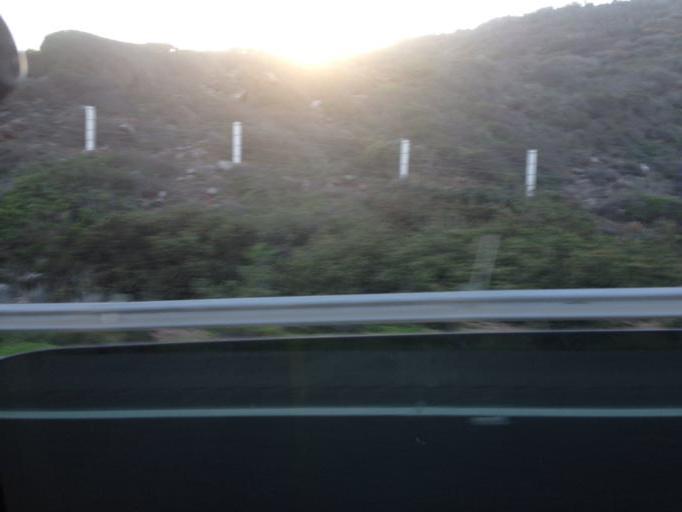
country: MX
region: Baja California
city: El Sauzal
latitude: 31.9145
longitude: -116.7531
